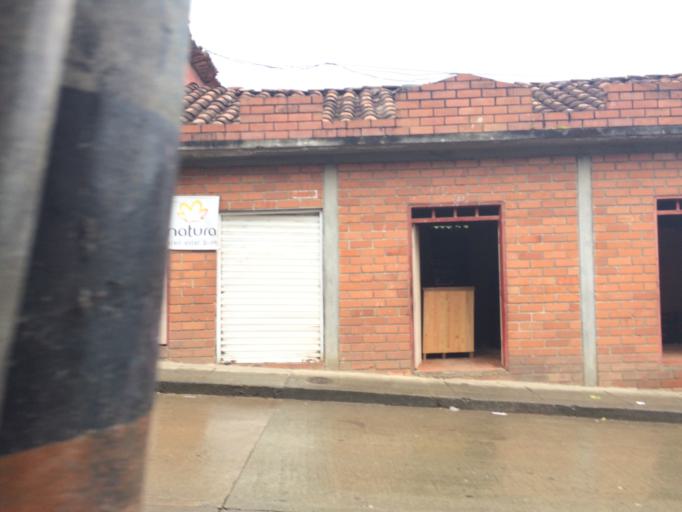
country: CO
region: Quindio
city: Genova
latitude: 4.2082
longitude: -75.7888
